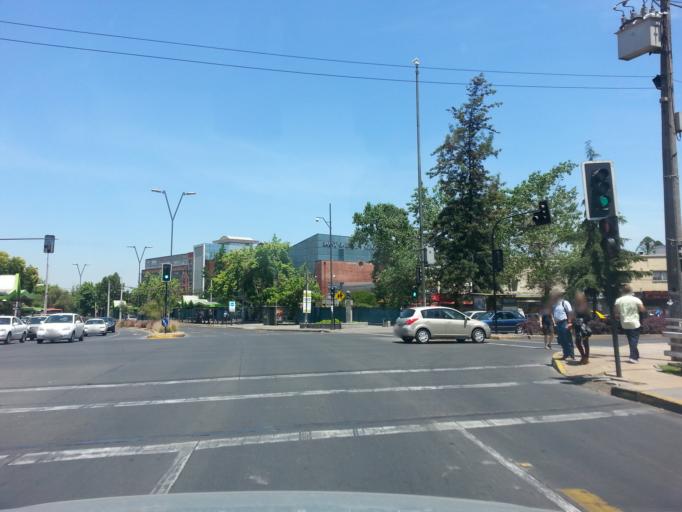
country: CL
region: Santiago Metropolitan
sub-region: Provincia de Santiago
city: Villa Presidente Frei, Nunoa, Santiago, Chile
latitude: -33.4317
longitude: -70.5846
